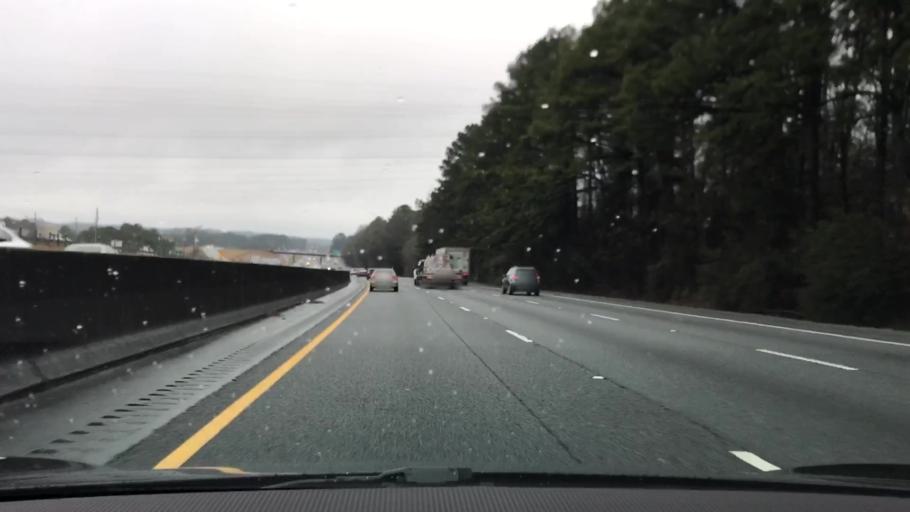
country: US
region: Georgia
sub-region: Newton County
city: Oxford
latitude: 33.6127
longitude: -83.8948
